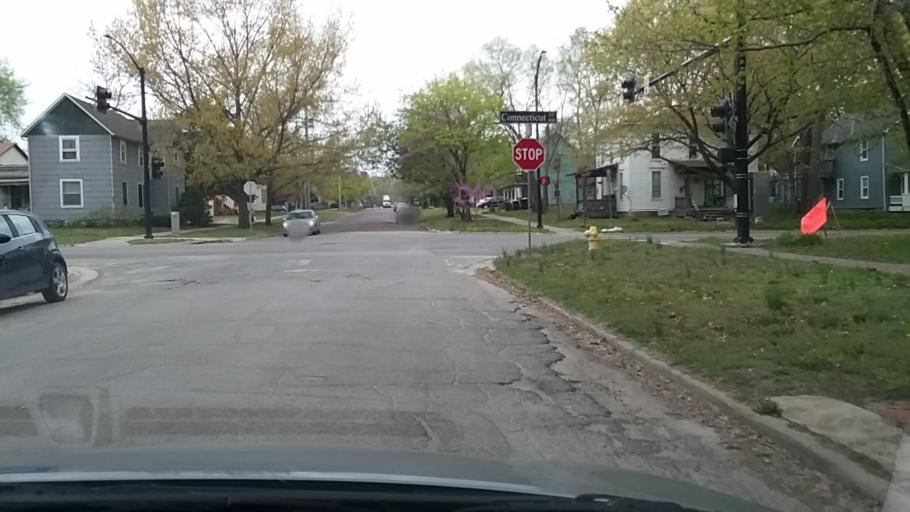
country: US
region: Kansas
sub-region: Douglas County
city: Lawrence
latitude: 38.9657
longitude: -95.2320
